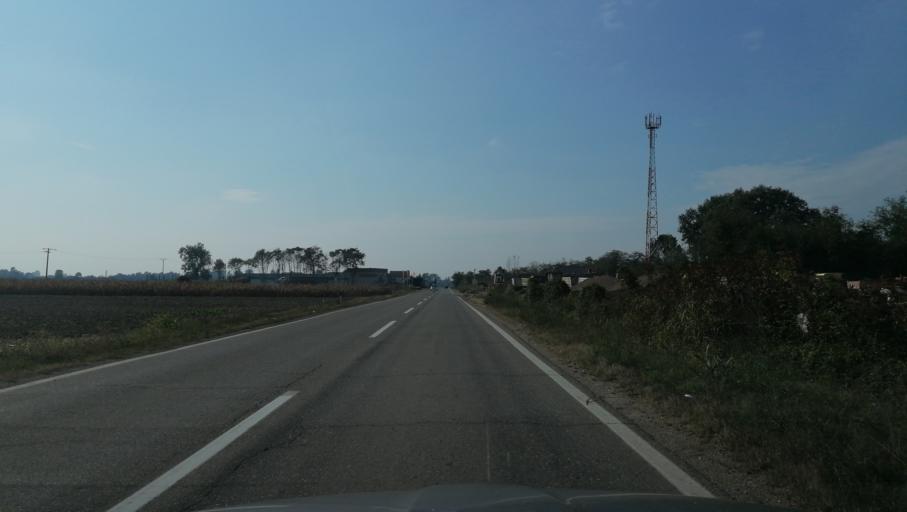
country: BA
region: Republika Srpska
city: Popovi
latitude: 44.7811
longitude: 19.3010
